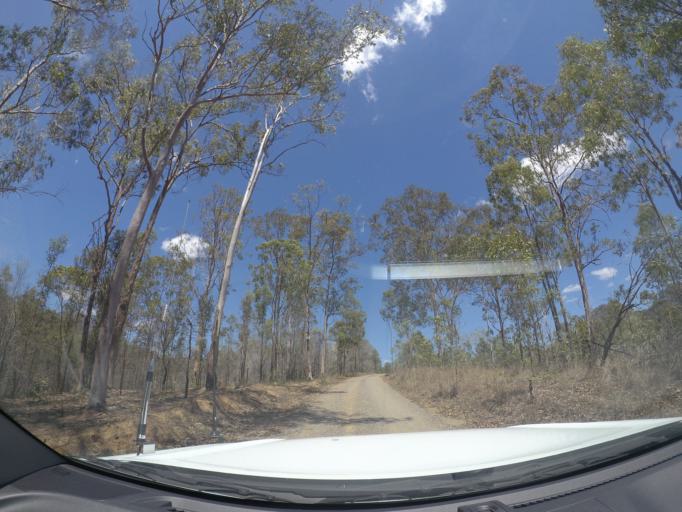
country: AU
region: Queensland
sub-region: Ipswich
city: Springfield Lakes
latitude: -27.8206
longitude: 152.8446
